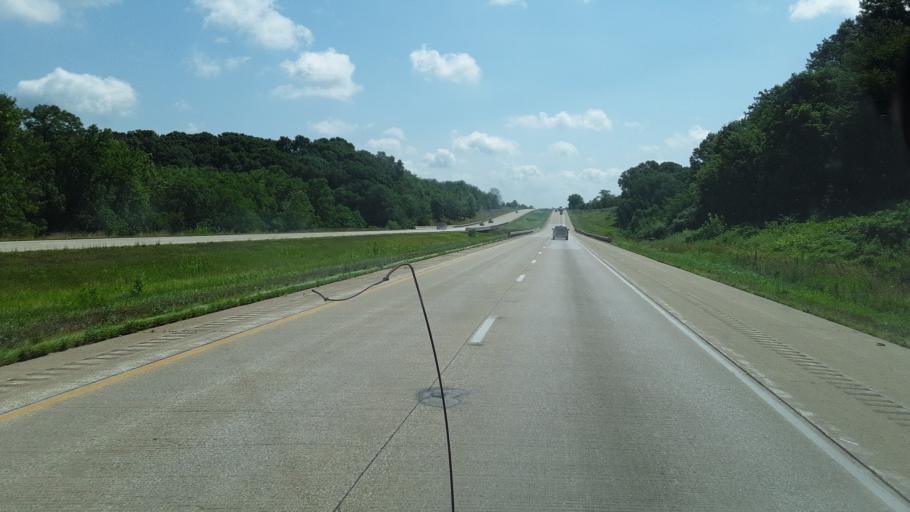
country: US
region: Illinois
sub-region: Clark County
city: Marshall
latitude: 39.4216
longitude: -87.6488
